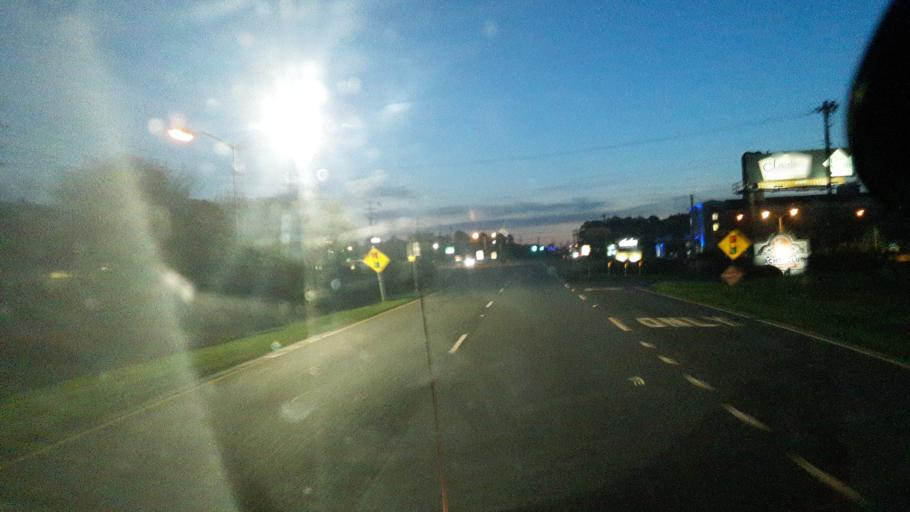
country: US
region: South Carolina
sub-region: Horry County
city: Little River
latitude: 33.8661
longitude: -78.6401
